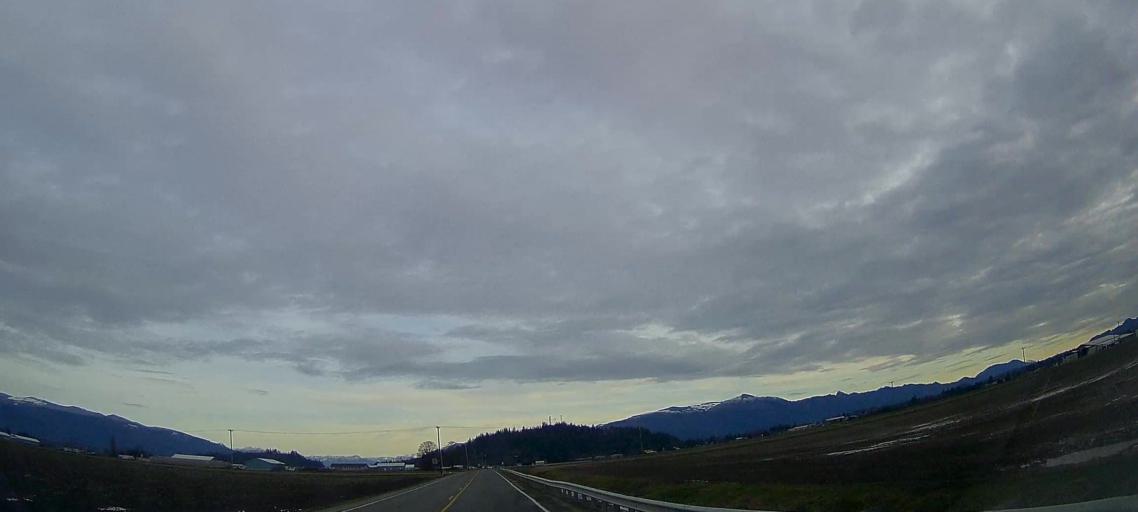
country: US
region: Washington
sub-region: Skagit County
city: Burlington
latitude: 48.4863
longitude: -122.3588
